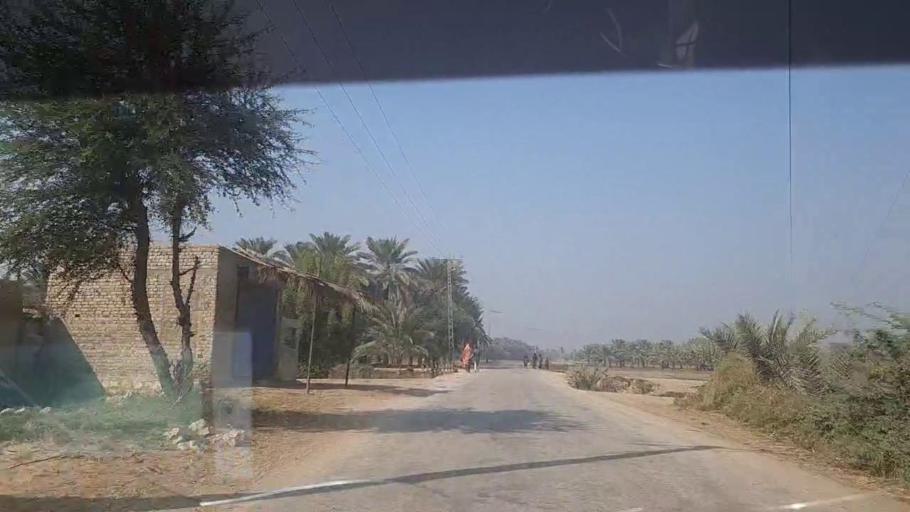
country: PK
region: Sindh
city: Kot Diji
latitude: 27.3658
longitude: 68.7031
